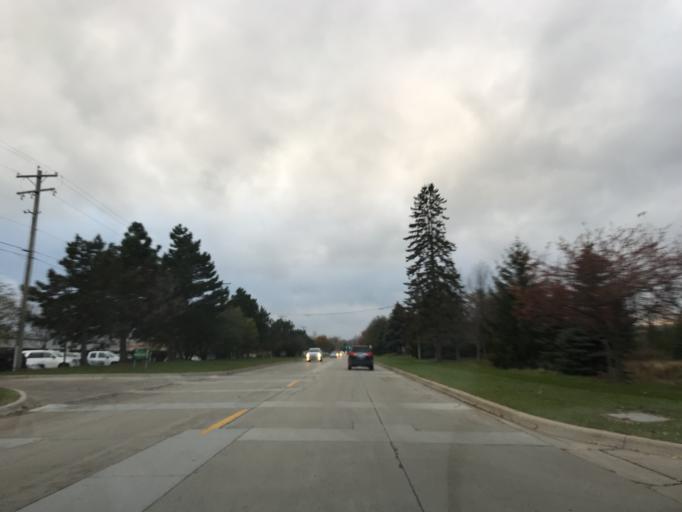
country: US
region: Michigan
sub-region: Oakland County
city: Novi
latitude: 42.4901
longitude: -83.4283
